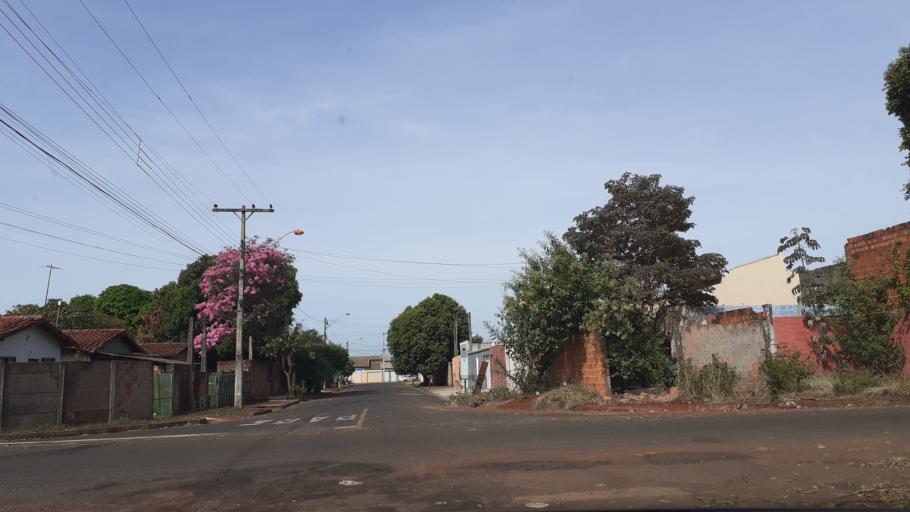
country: BR
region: Goias
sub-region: Itumbiara
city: Itumbiara
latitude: -18.4216
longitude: -49.2456
